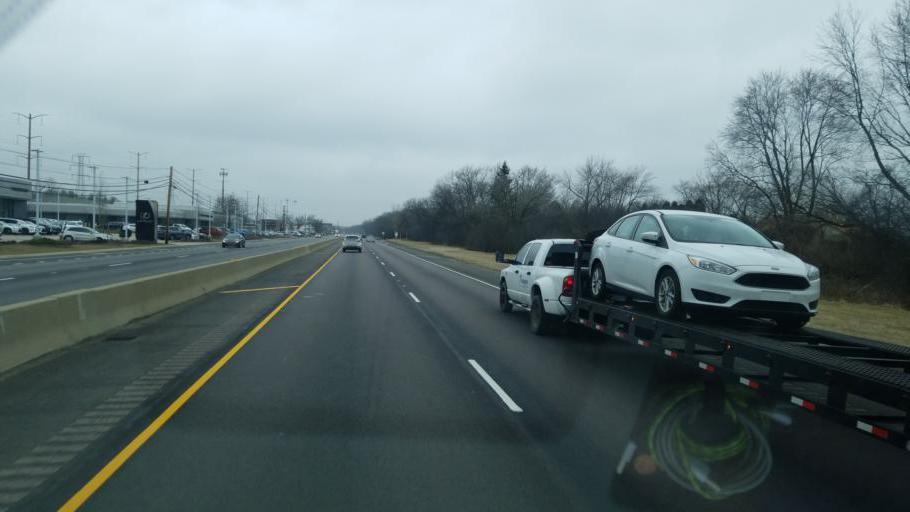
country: US
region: Illinois
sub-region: Lake County
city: Highwood
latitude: 42.2062
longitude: -87.8368
